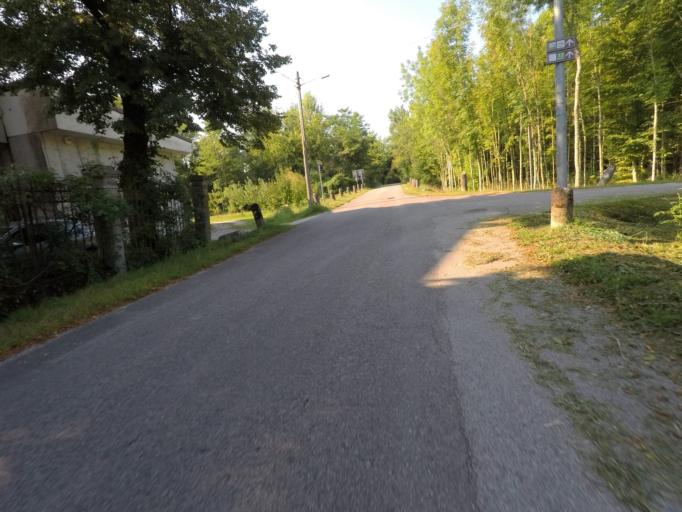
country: IT
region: Friuli Venezia Giulia
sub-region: Provincia di Pordenone
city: Pinzano al Tagliamento
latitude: 46.1952
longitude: 12.9559
